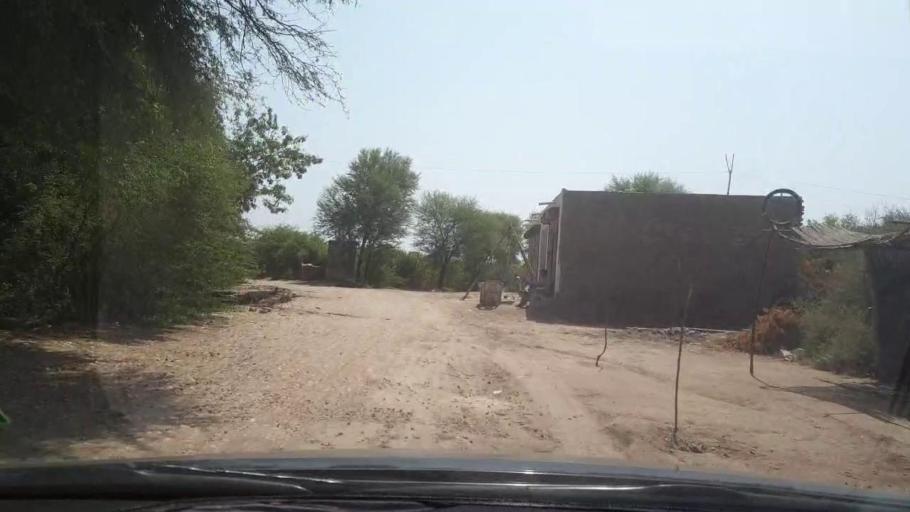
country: PK
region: Sindh
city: Naukot
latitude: 24.7686
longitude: 69.1952
